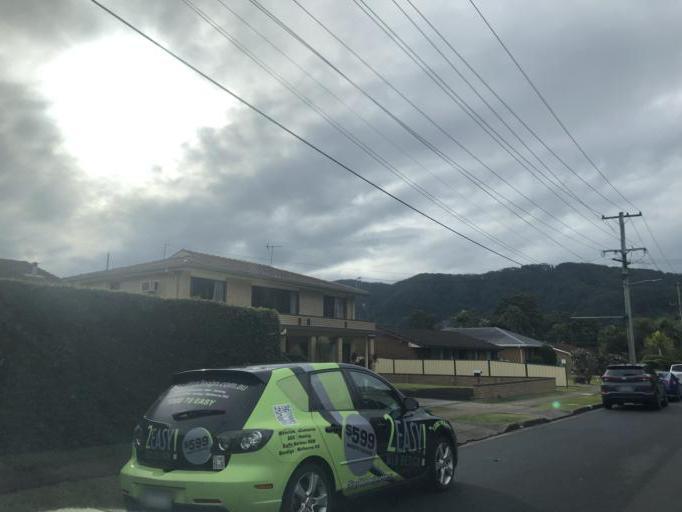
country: AU
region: New South Wales
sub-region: Coffs Harbour
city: Coffs Harbour
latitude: -30.2848
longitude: 153.1113
